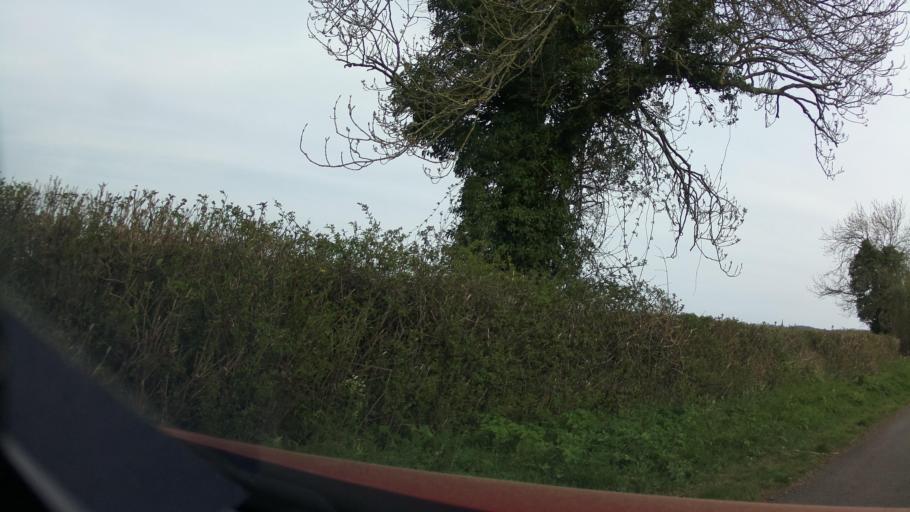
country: GB
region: England
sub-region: Somerset
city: Milborne Port
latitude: 50.9732
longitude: -2.4686
